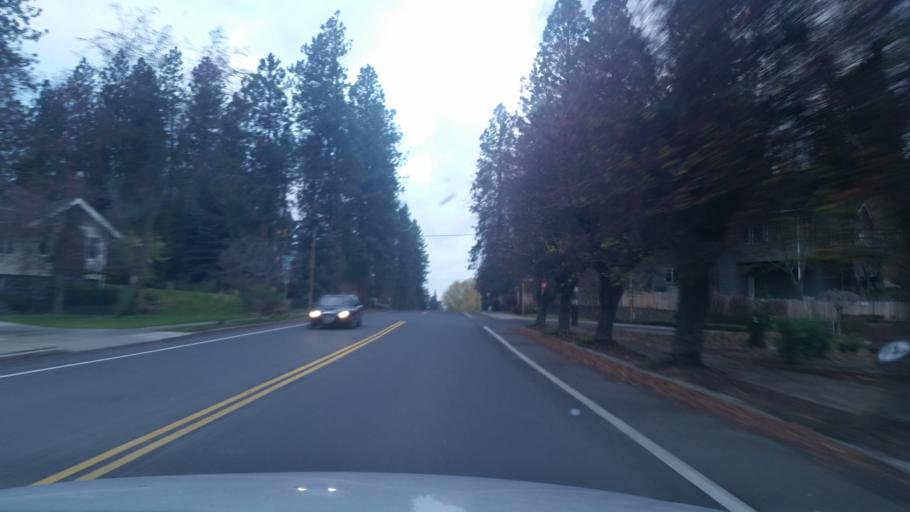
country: US
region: Washington
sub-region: Spokane County
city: Spokane
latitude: 47.6404
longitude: -117.3934
